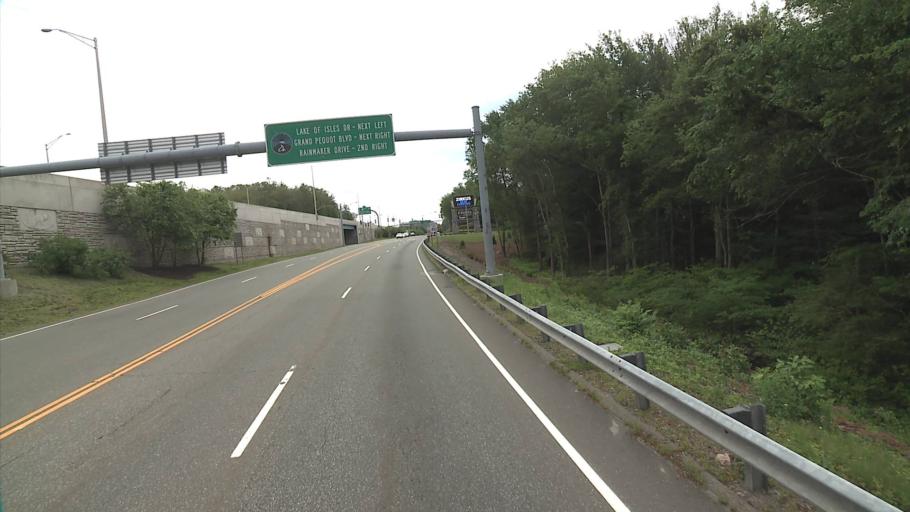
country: US
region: Connecticut
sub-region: New London County
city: Preston City
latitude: 41.4765
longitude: -71.9574
